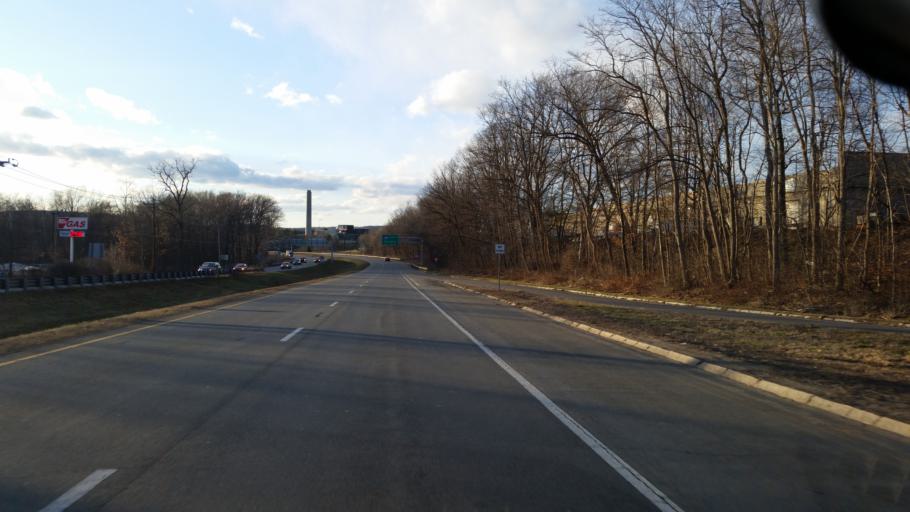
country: US
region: Massachusetts
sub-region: Essex County
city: Haverhill
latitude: 42.7572
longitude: -71.1154
